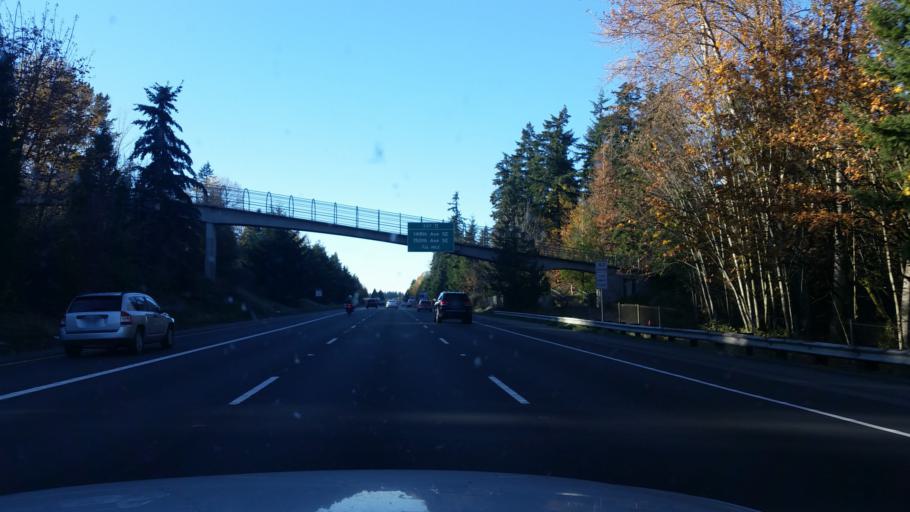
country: US
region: Washington
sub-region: King County
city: West Lake Sammamish
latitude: 47.5704
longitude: -122.1099
